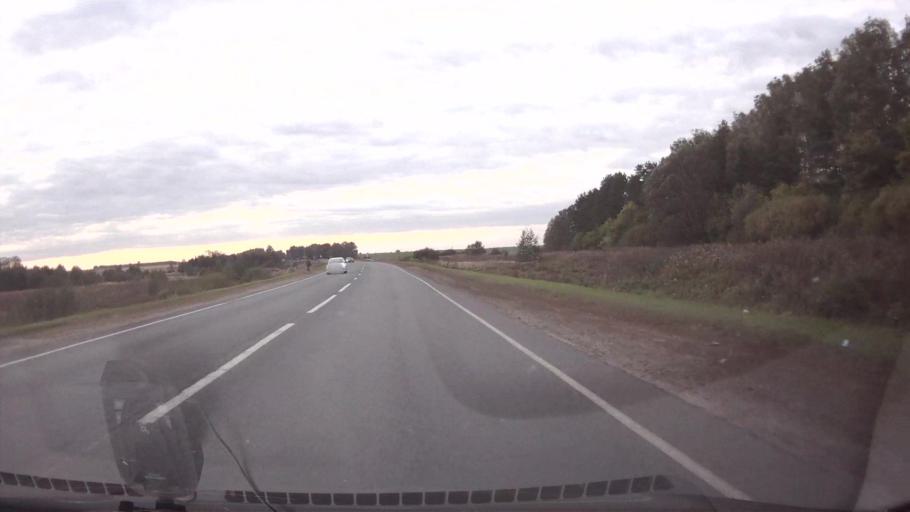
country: RU
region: Mariy-El
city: Sovetskiy
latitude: 56.7472
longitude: 48.3278
